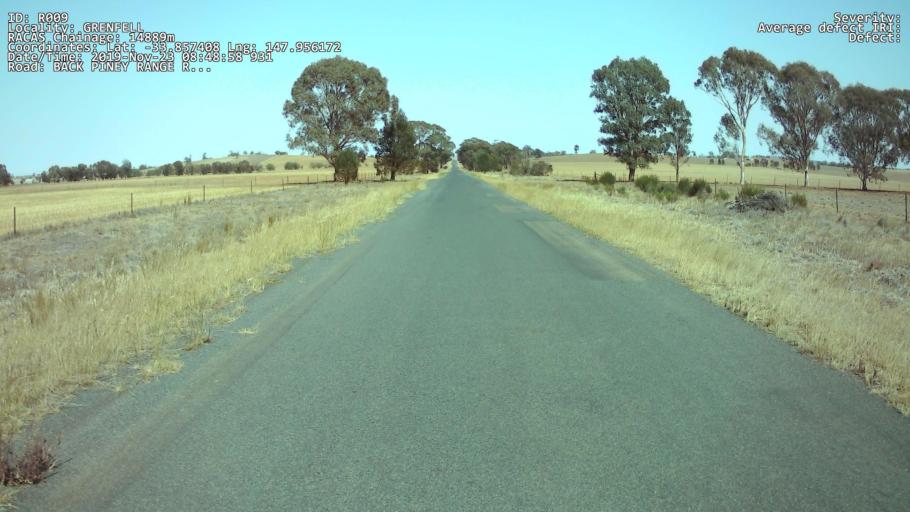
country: AU
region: New South Wales
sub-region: Weddin
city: Grenfell
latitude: -33.8574
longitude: 147.9562
